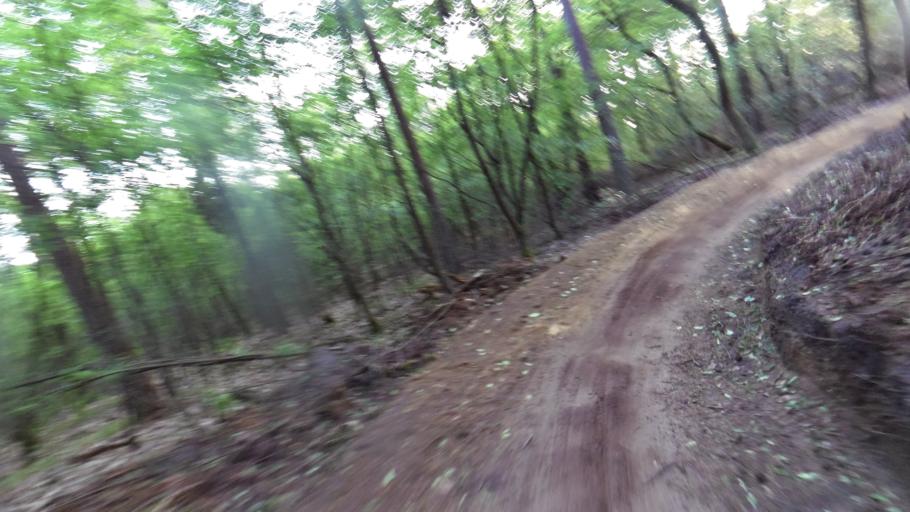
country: NL
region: Gelderland
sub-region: Gemeente Ede
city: Ede
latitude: 52.0599
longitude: 5.6654
